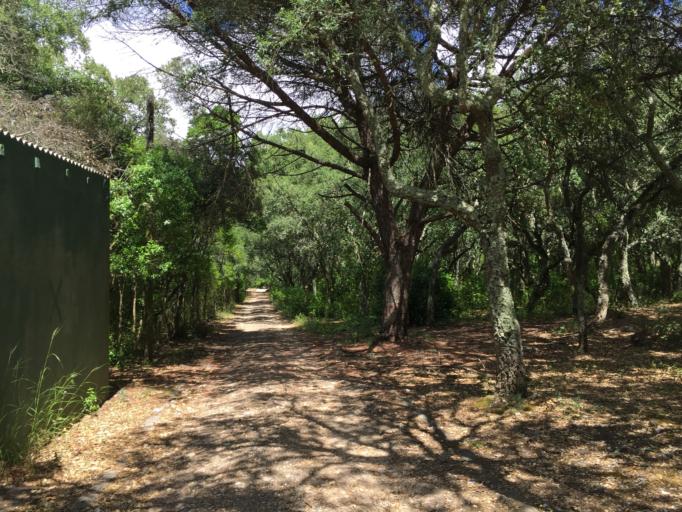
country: PT
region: Lisbon
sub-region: Odivelas
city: Pontinha
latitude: 38.7382
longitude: -9.1914
